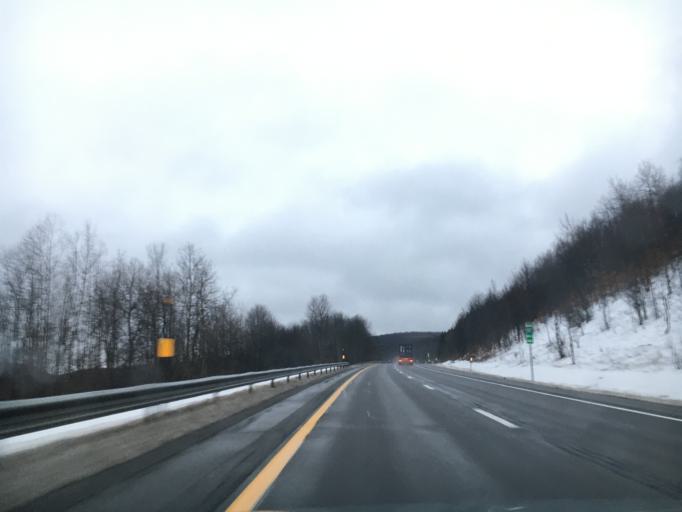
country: US
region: New York
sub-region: Cortland County
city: McGraw
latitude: 42.5104
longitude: -76.0787
